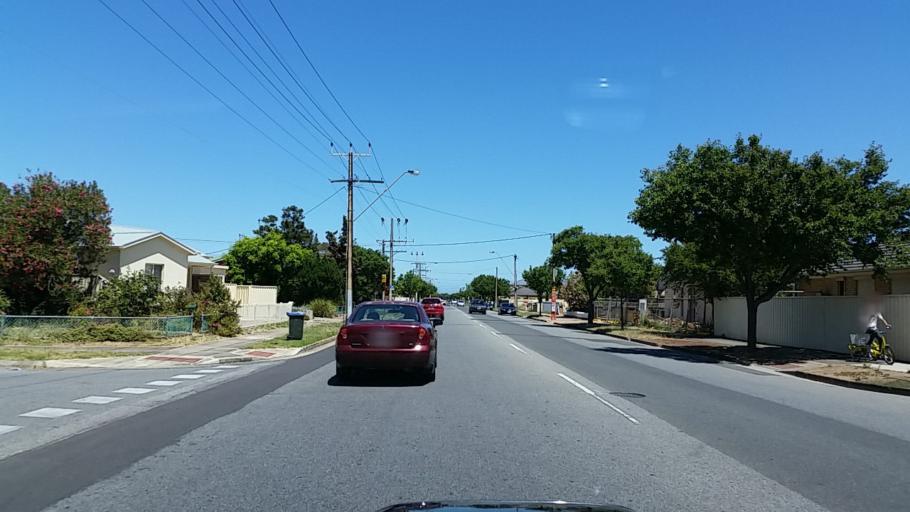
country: AU
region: South Australia
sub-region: Charles Sturt
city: Woodville West
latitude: -34.8912
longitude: 138.5282
